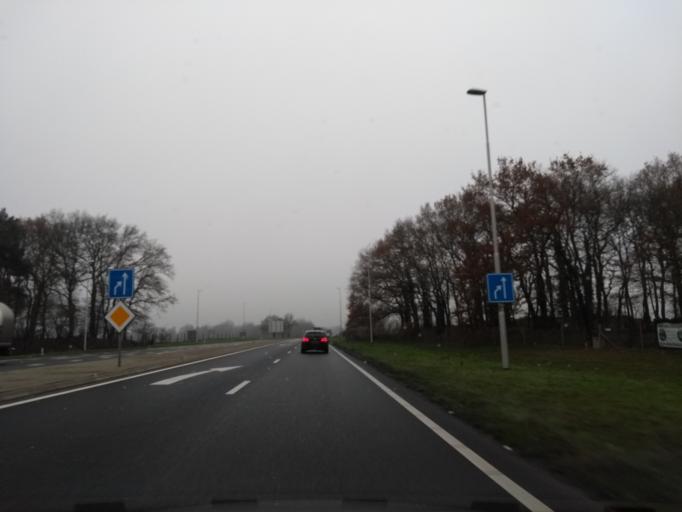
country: NL
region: Overijssel
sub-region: Gemeente Twenterand
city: Vroomshoop
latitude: 52.5103
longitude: 6.5628
